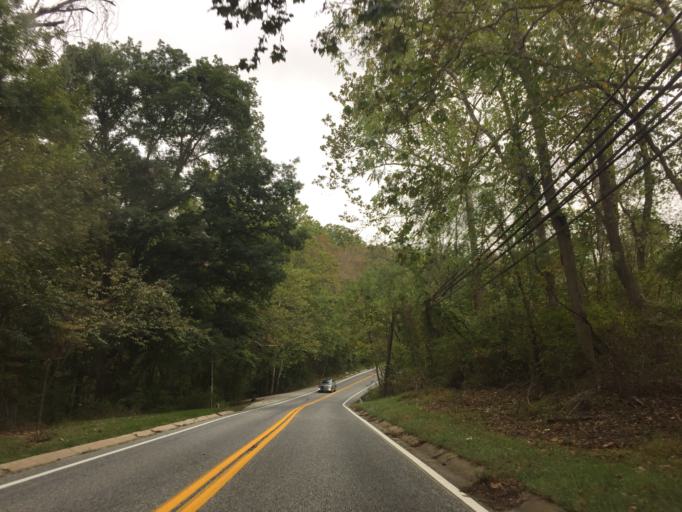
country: US
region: Maryland
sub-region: Baltimore County
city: Hunt Valley
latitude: 39.4919
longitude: -76.5962
